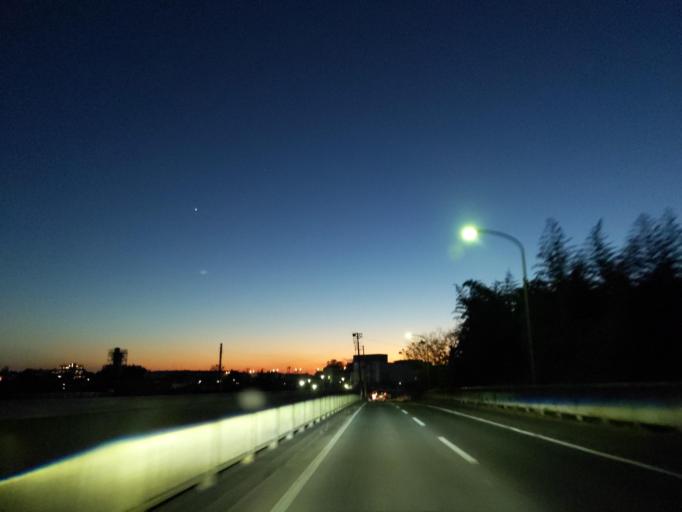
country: JP
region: Fukushima
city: Sukagawa
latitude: 37.3069
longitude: 140.3802
